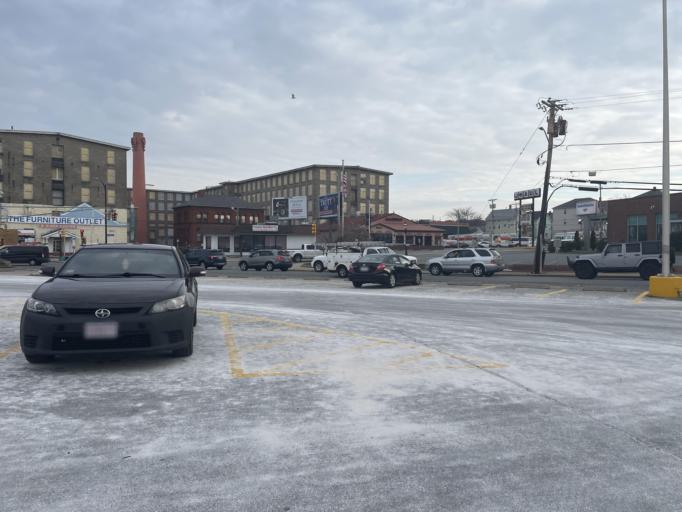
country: US
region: Massachusetts
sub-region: Bristol County
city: Fall River
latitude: 41.6948
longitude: -71.1401
